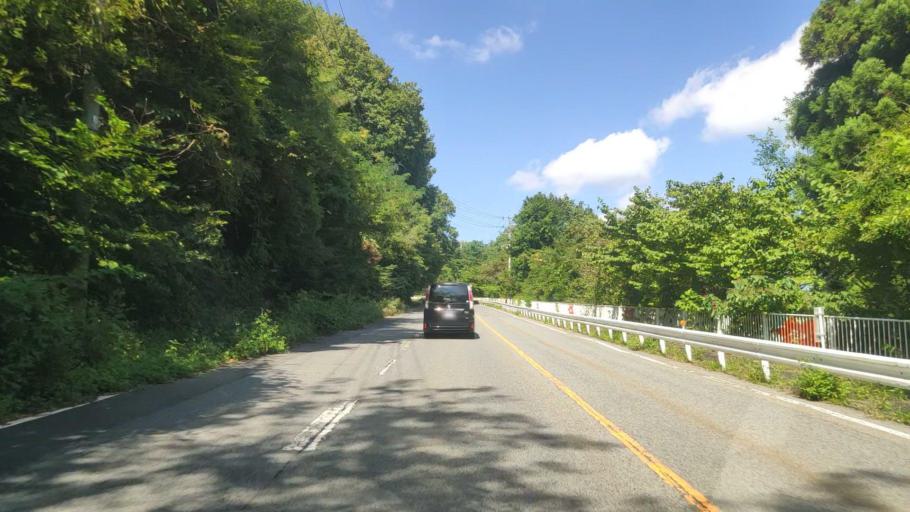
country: JP
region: Gunma
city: Shibukawa
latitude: 36.4977
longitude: 138.9127
